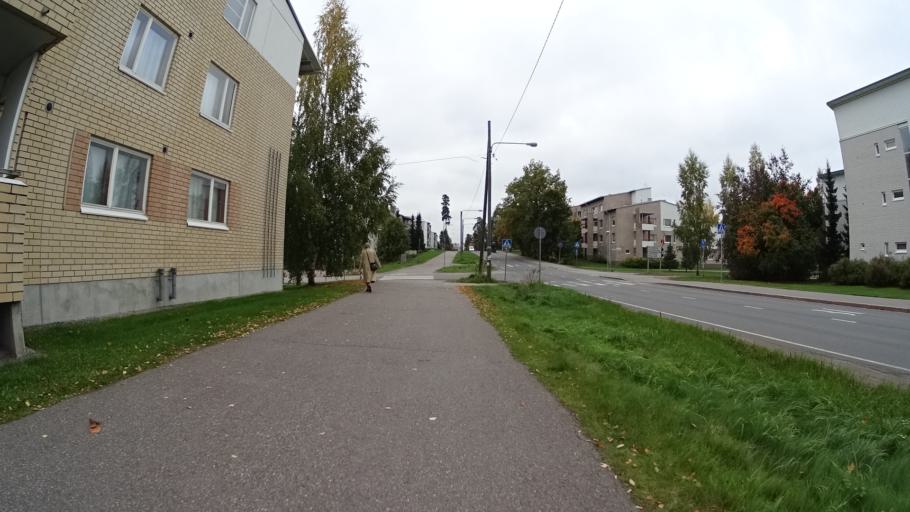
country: FI
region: Uusimaa
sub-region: Helsinki
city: Kilo
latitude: 60.2312
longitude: 24.8139
